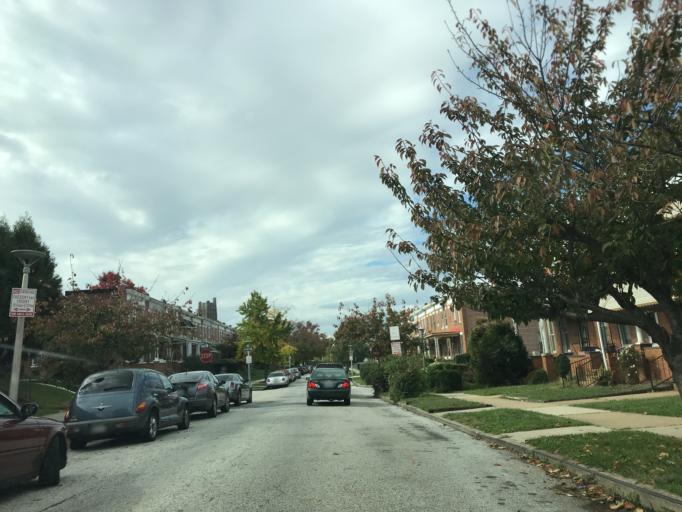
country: US
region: Maryland
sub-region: City of Baltimore
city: Baltimore
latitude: 39.3268
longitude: -76.5913
